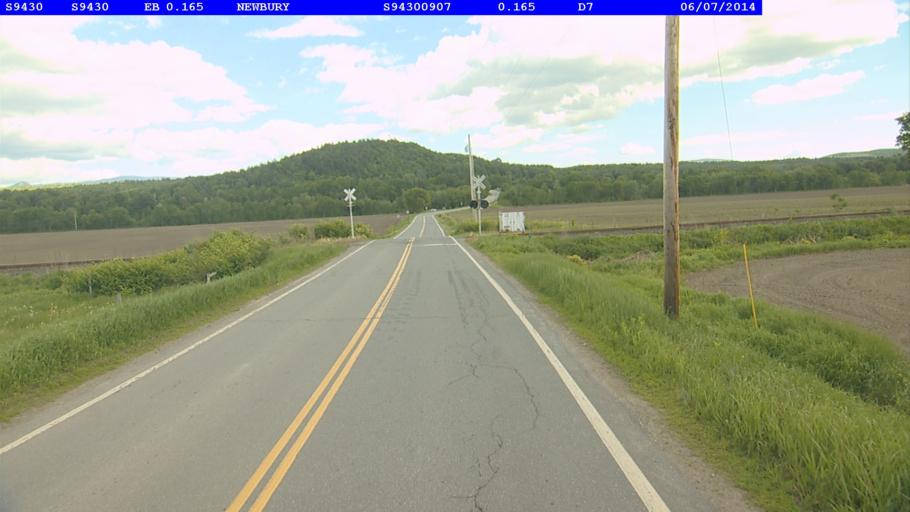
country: US
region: New Hampshire
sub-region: Grafton County
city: North Haverhill
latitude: 44.0695
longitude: -72.0557
